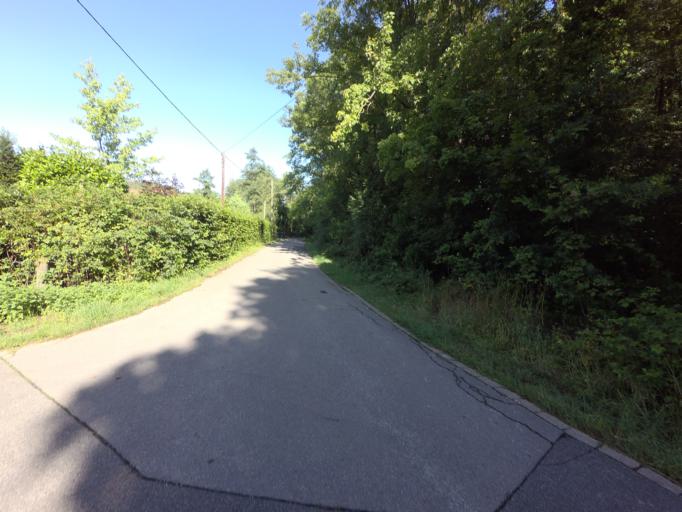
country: DE
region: North Rhine-Westphalia
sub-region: Regierungsbezirk Koln
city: Herzogenrath
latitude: 50.8449
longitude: 6.0976
